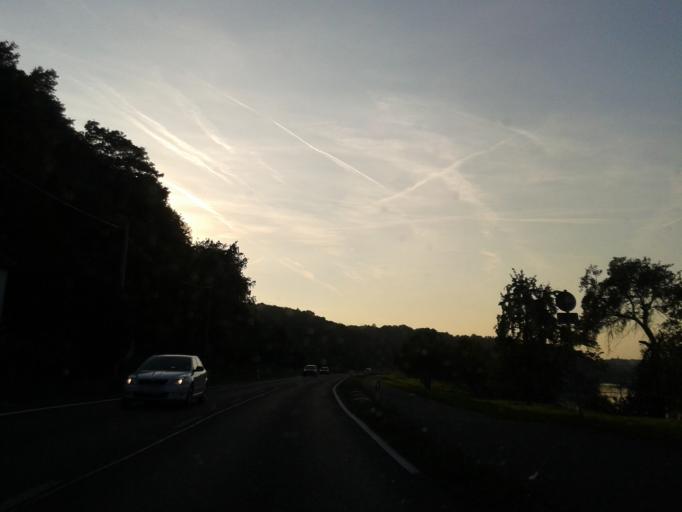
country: DE
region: Saxony
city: Meissen
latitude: 51.1881
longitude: 13.4321
